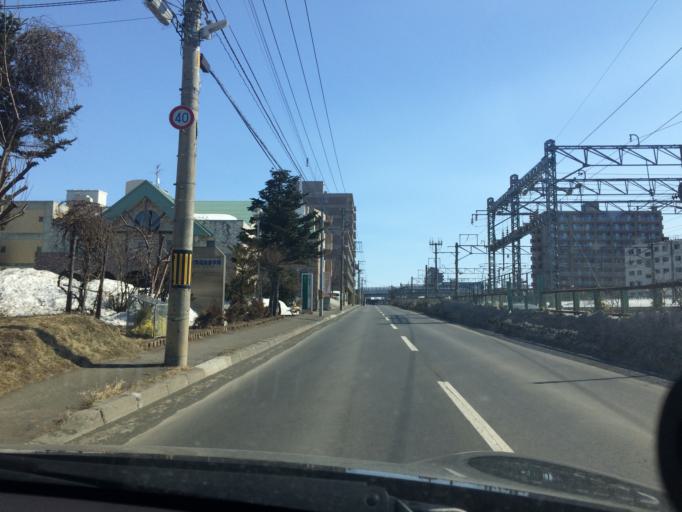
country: JP
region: Hokkaido
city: Sapporo
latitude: 43.0589
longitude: 141.4075
